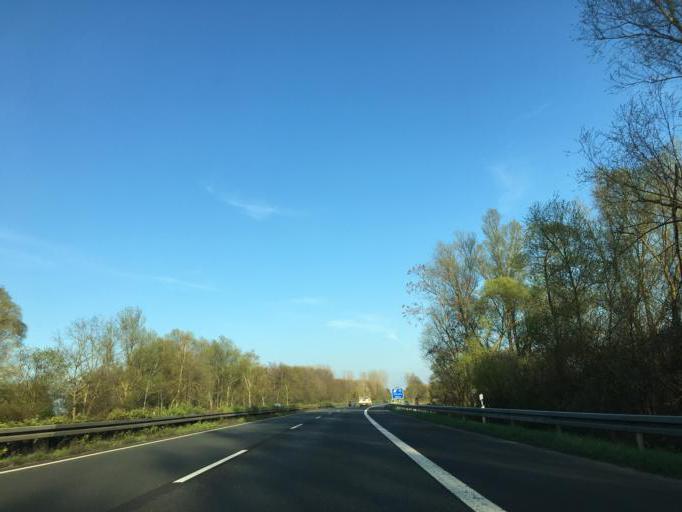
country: DE
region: Hesse
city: Bruchkobel
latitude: 50.1545
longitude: 8.9344
